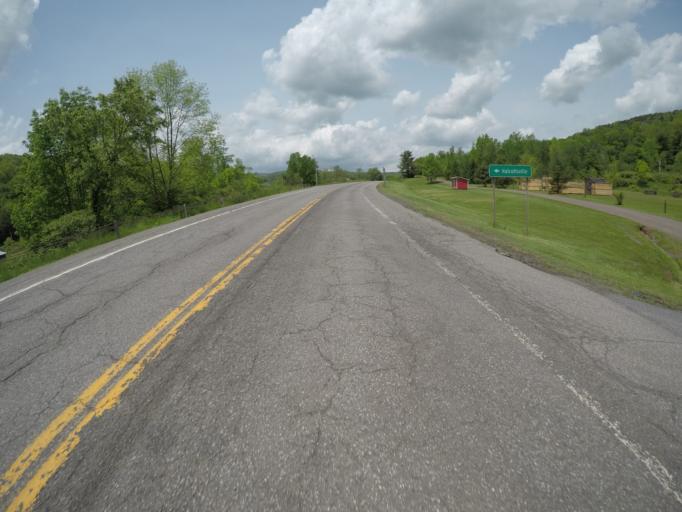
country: US
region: New York
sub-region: Delaware County
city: Stamford
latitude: 42.2019
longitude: -74.5995
